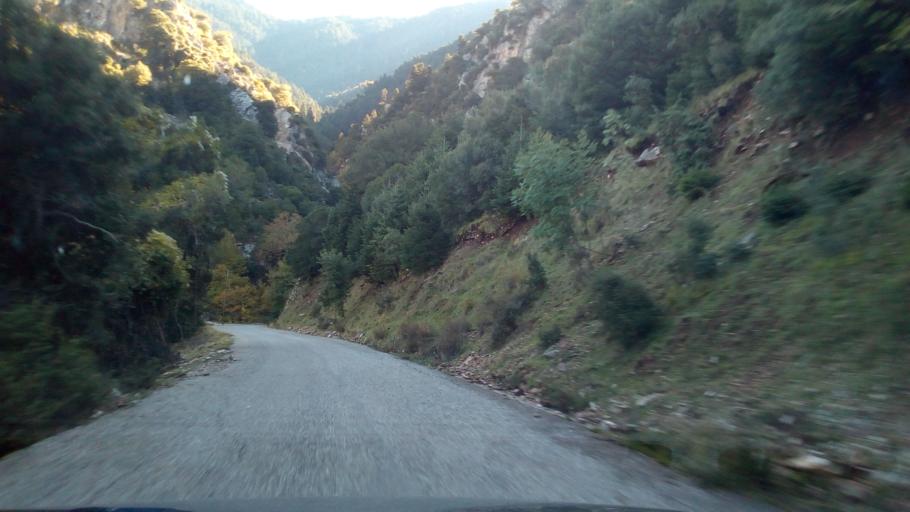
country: GR
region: West Greece
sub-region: Nomos Aitolias kai Akarnanias
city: Nafpaktos
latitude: 38.5545
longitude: 21.8570
